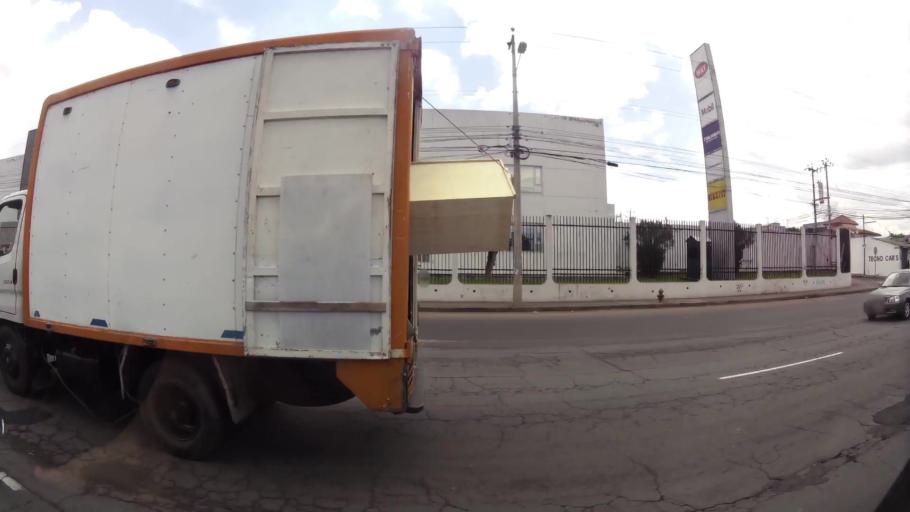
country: EC
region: Pichincha
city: Quito
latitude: -0.1064
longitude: -78.4399
